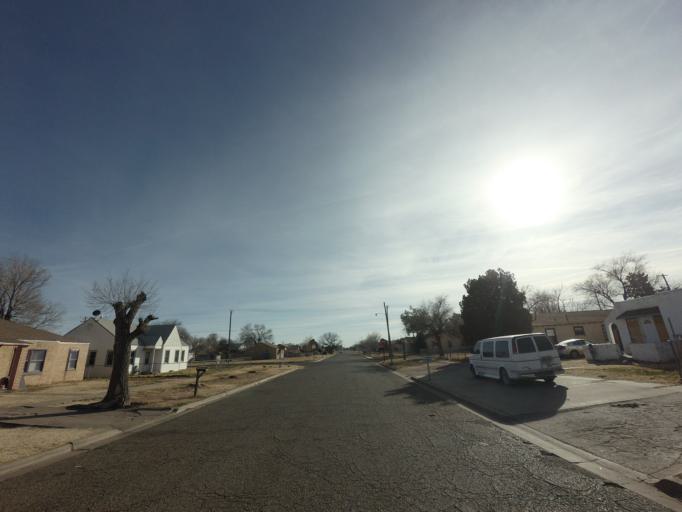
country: US
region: New Mexico
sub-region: Curry County
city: Clovis
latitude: 34.4072
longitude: -103.2180
